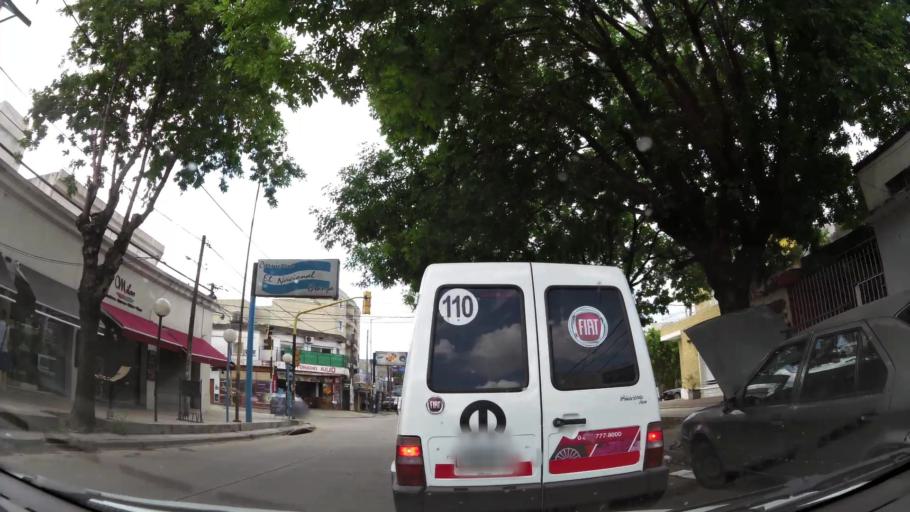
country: AR
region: Buenos Aires
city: Ituzaingo
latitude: -34.6377
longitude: -58.6553
